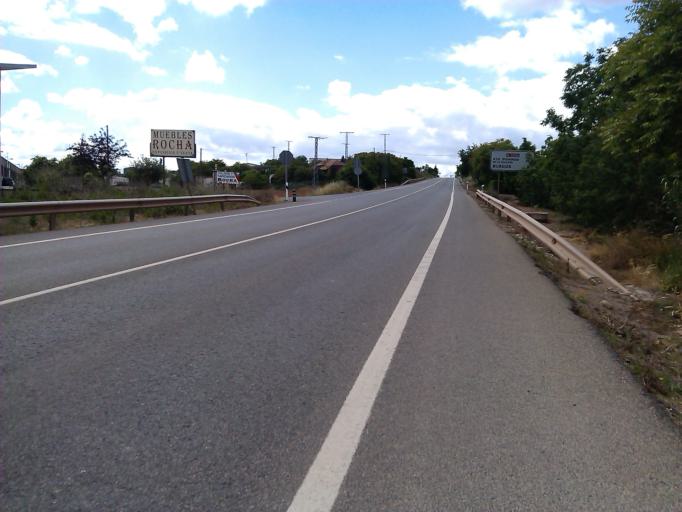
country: ES
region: La Rioja
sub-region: Provincia de La Rioja
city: Najera
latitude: 42.4247
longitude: -2.7378
